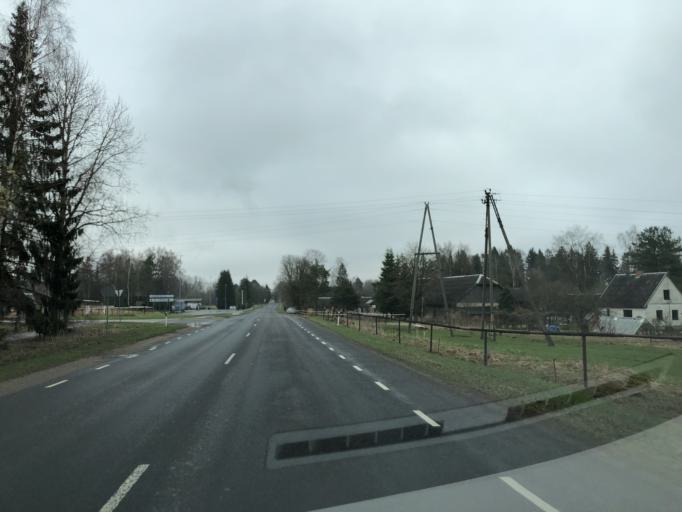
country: EE
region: Laeaene-Virumaa
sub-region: Vaeike-Maarja vald
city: Vaike-Maarja
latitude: 59.1089
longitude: 26.2352
